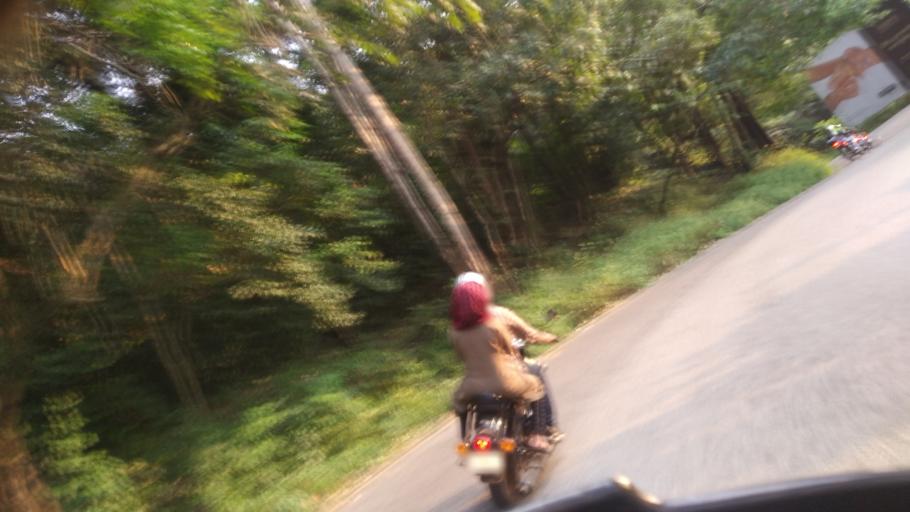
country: IN
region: Kerala
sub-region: Wayanad
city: Kalpetta
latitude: 11.5018
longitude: 76.0229
